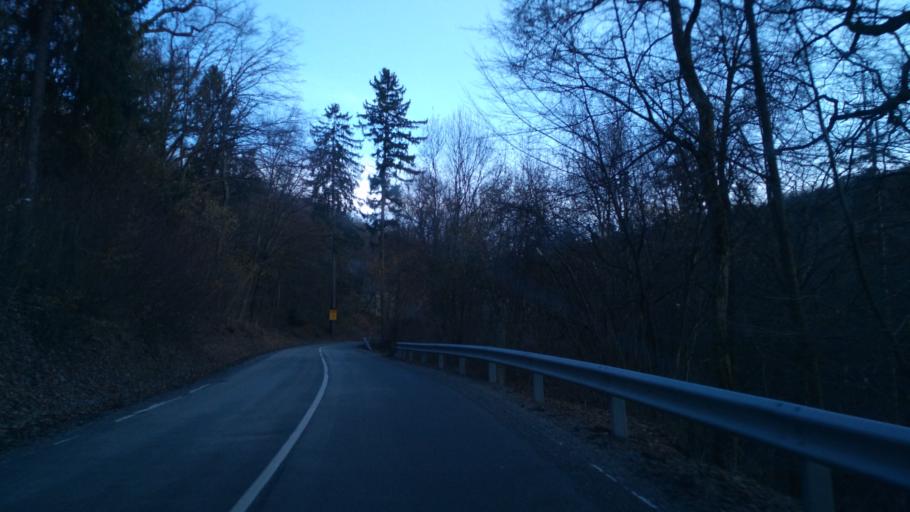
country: SK
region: Kosicky
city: Kosice
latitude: 48.7492
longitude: 21.2073
